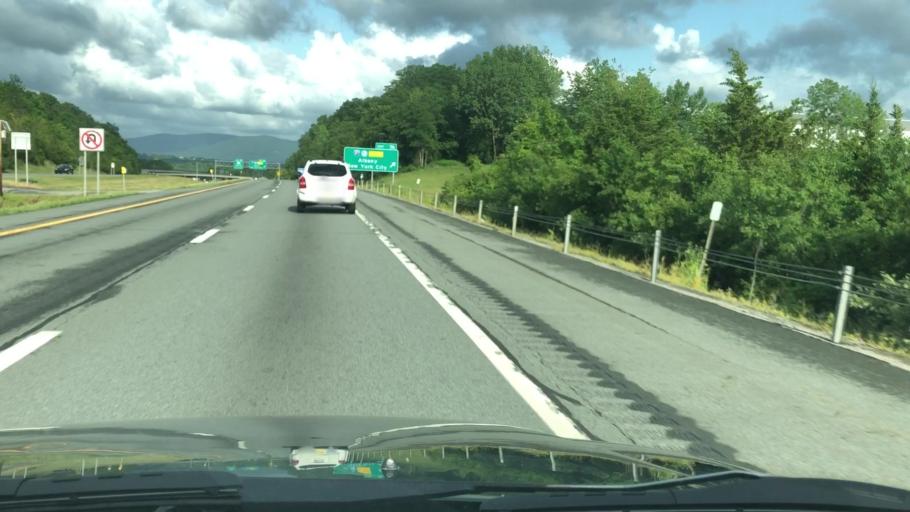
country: US
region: New York
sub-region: Orange County
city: Gardnertown
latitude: 41.5153
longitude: -74.0808
